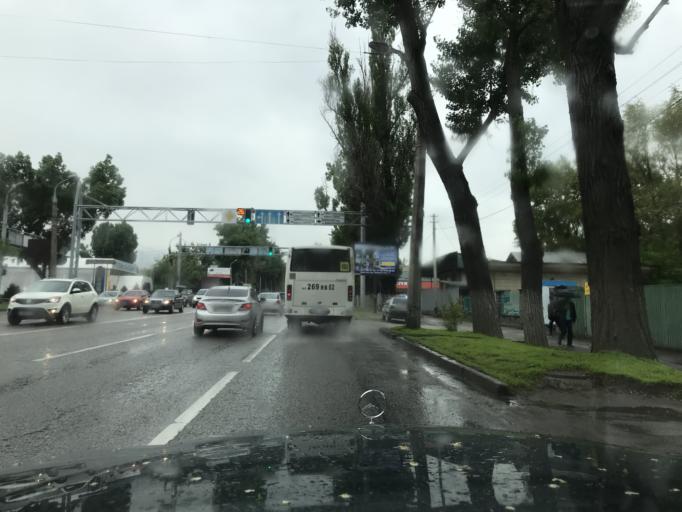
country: KZ
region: Almaty Qalasy
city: Almaty
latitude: 43.2869
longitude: 76.9476
